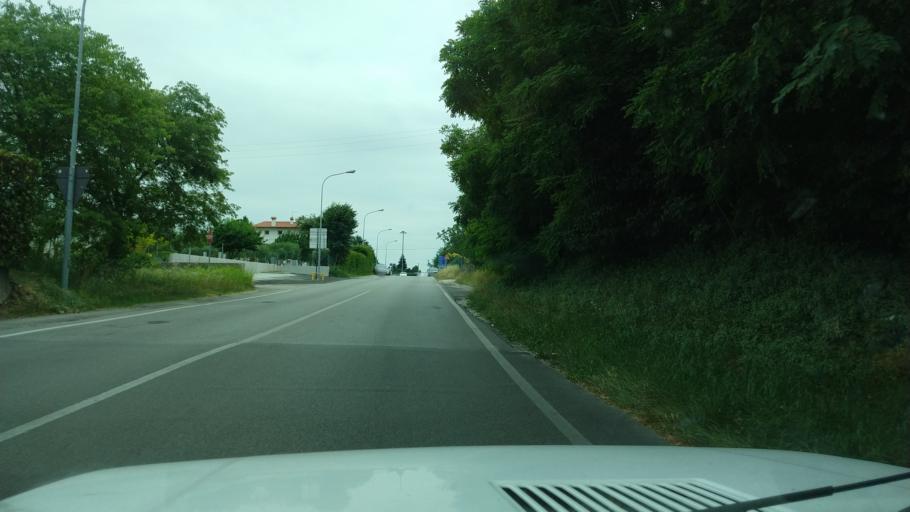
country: IT
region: Veneto
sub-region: Provincia di Vicenza
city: Bassano del Grappa
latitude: 45.7484
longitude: 11.7239
